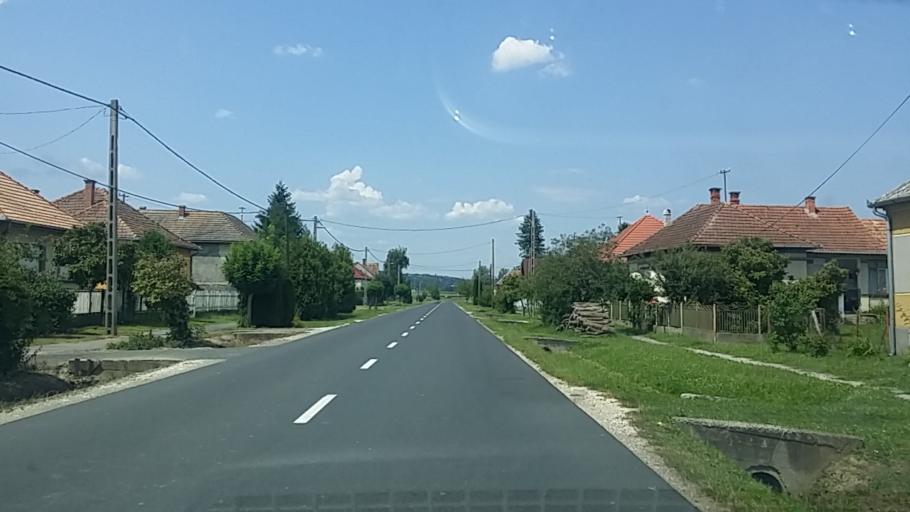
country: HR
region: Medimurska
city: Podturen
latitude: 46.5257
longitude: 16.5552
